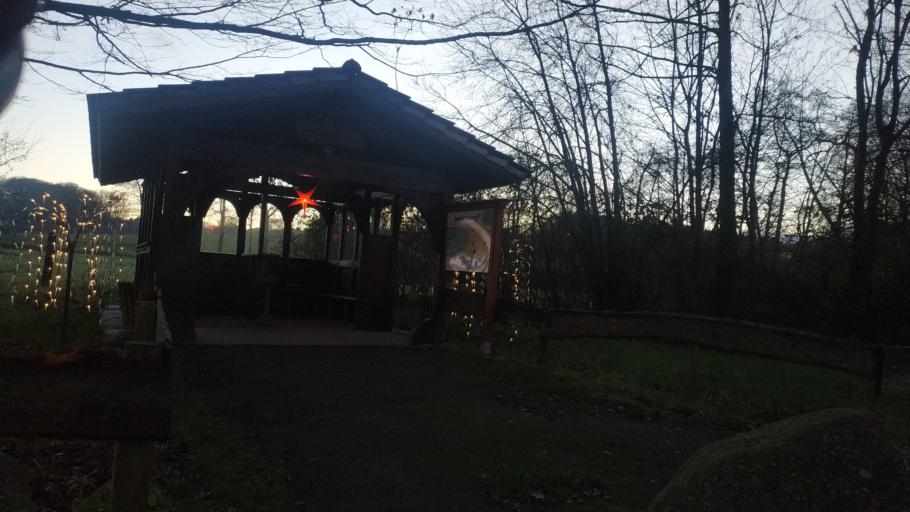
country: DE
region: North Rhine-Westphalia
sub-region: Regierungsbezirk Munster
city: Mettingen
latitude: 52.3206
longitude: 7.7623
